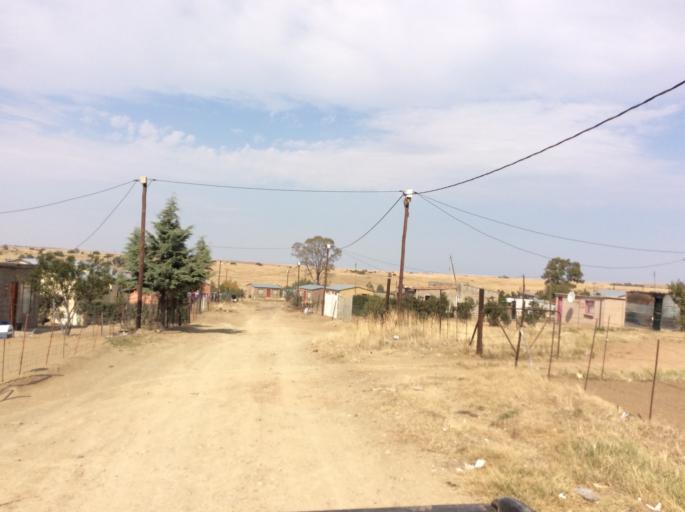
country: ZA
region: Orange Free State
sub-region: Xhariep District Municipality
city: Dewetsdorp
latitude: -29.5963
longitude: 26.6812
